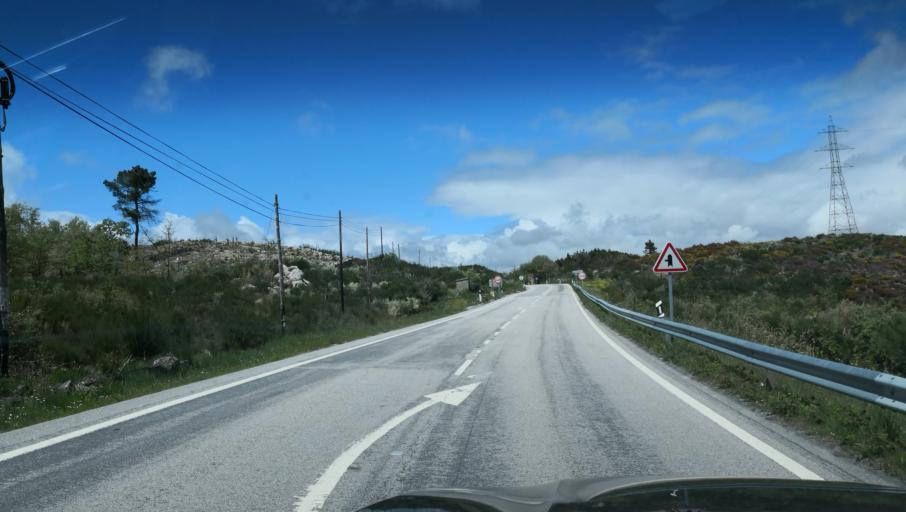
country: PT
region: Vila Real
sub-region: Vila Real
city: Vila Real
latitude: 41.3947
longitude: -7.7015
